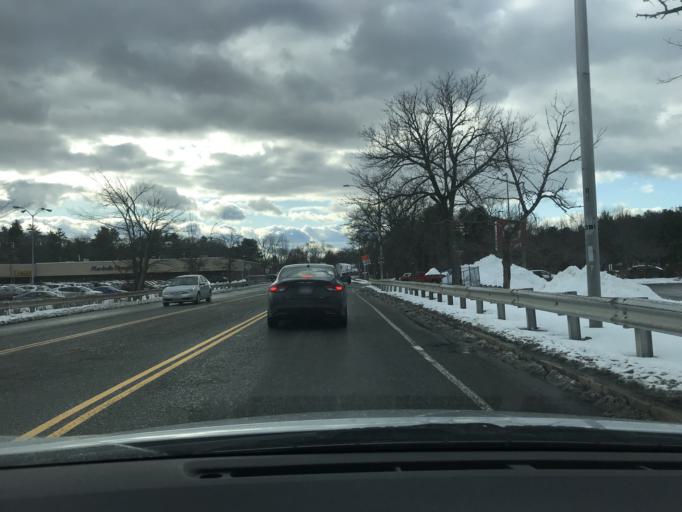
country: US
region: Massachusetts
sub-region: Essex County
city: Saugus
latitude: 42.4806
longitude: -71.0236
